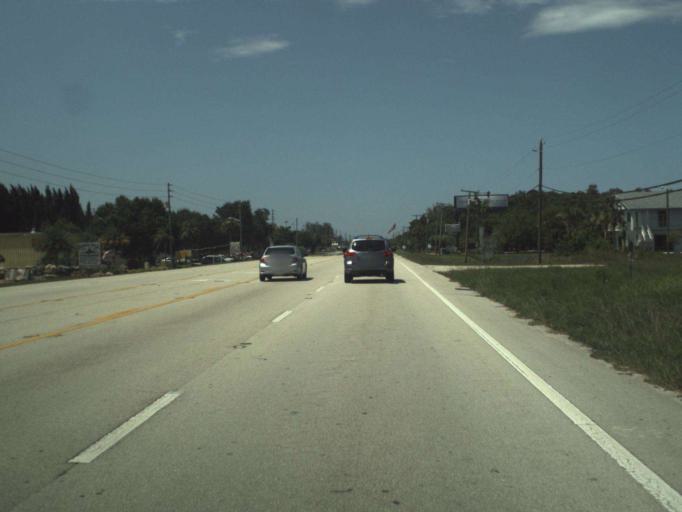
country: US
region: Florida
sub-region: Saint Lucie County
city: White City
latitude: 27.3870
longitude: -80.3257
